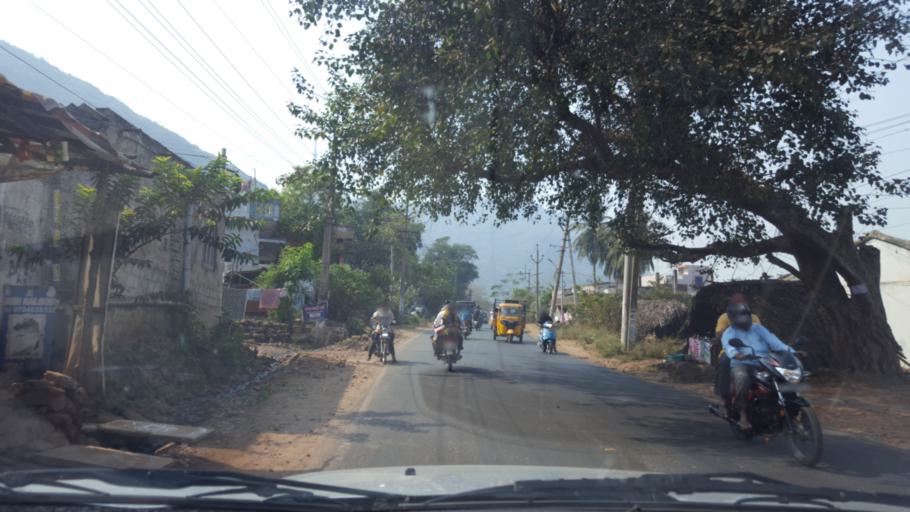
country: IN
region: Andhra Pradesh
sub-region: Vishakhapatnam
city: Vepagunta
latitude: 17.7760
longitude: 83.2497
